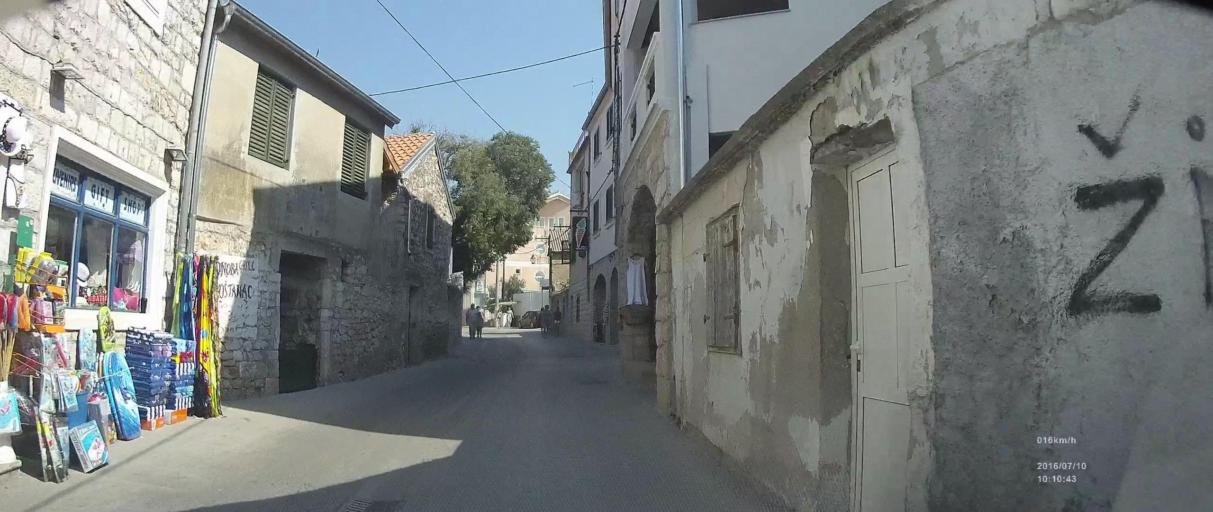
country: HR
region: Zadarska
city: Pakostane
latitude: 43.9078
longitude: 15.5081
